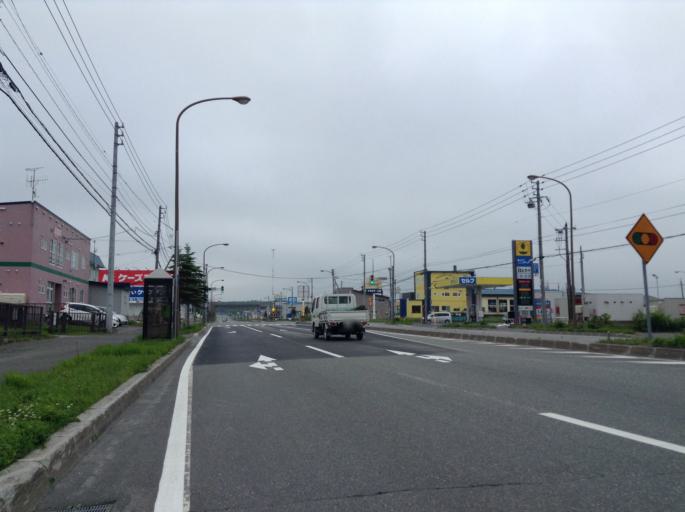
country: JP
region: Hokkaido
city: Wakkanai
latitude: 45.3837
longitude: 141.7078
